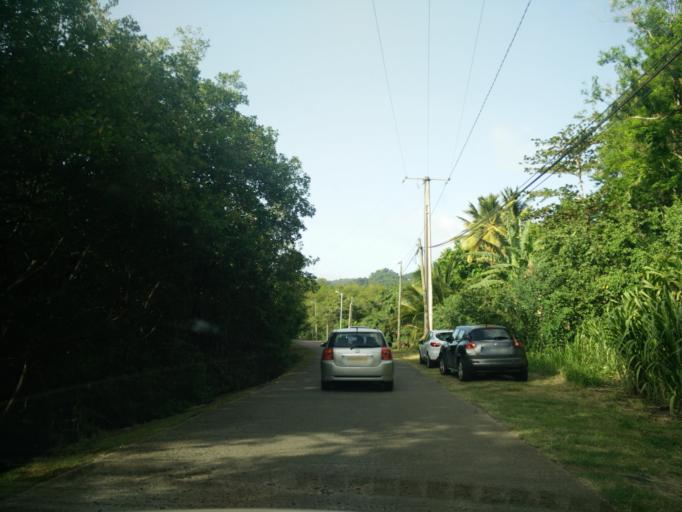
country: MQ
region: Martinique
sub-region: Martinique
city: Riviere-Pilote
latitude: 14.4669
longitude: -60.9096
